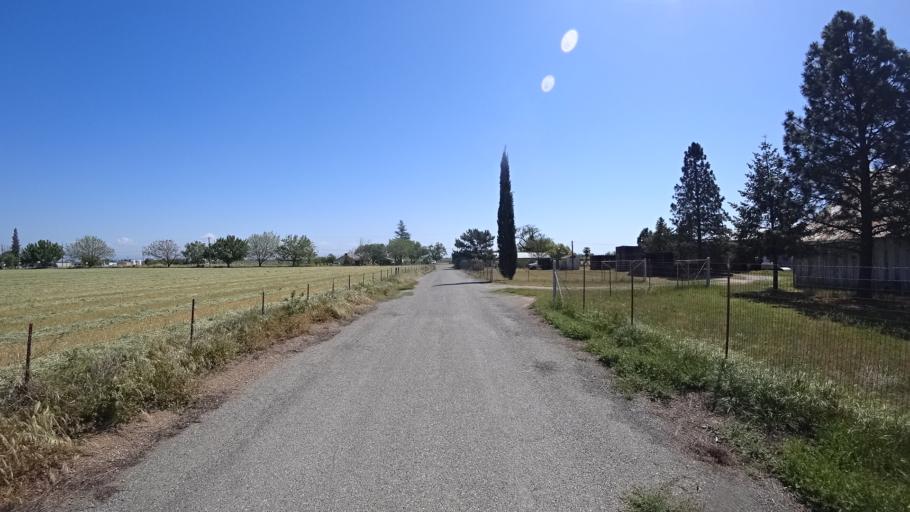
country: US
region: California
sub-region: Glenn County
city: Orland
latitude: 39.7666
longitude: -122.1612
